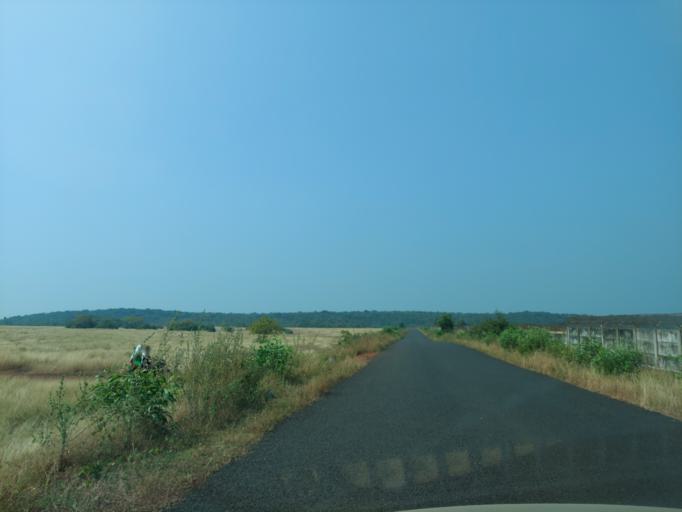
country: IN
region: Maharashtra
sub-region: Sindhudurg
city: Malvan
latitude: 15.9985
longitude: 73.5115
